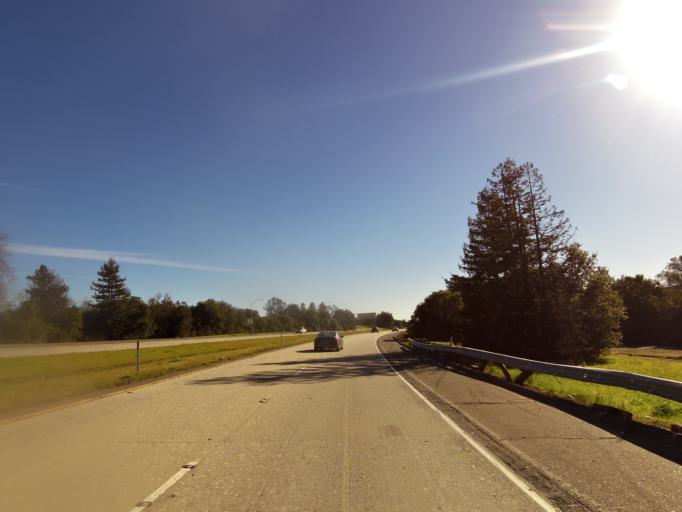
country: US
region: California
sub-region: Sonoma County
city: Cloverdale
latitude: 38.7584
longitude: -122.9746
